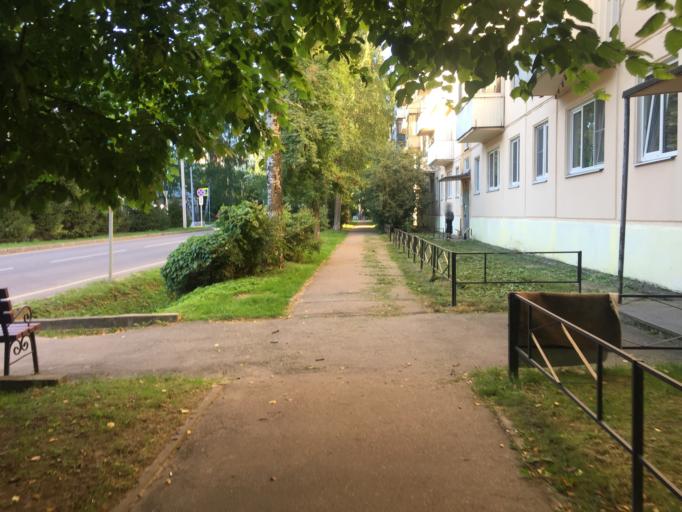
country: RU
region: Leningrad
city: Murino
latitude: 60.0382
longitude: 30.4652
